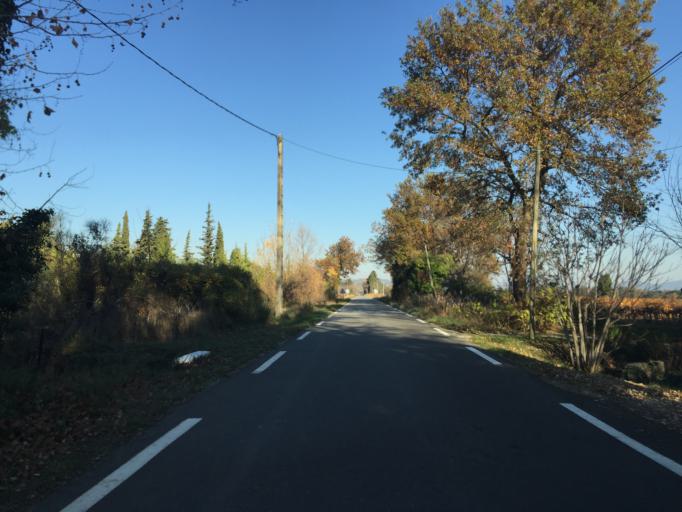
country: FR
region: Provence-Alpes-Cote d'Azur
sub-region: Departement du Vaucluse
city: Camaret-sur-Aigues
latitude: 44.1991
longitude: 4.9079
